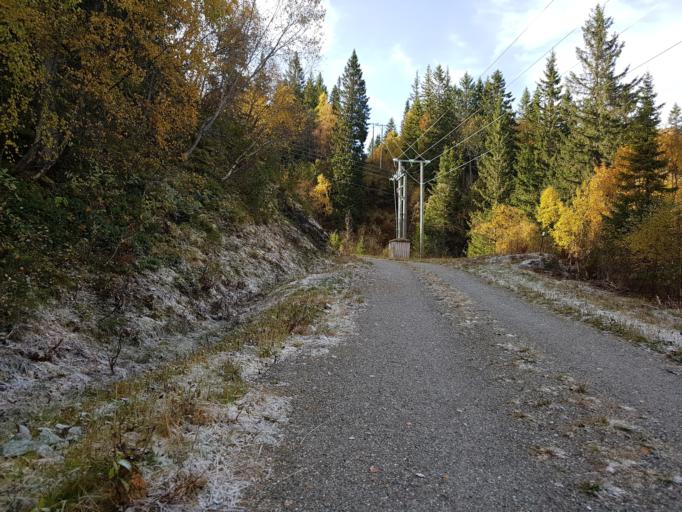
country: NO
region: Sor-Trondelag
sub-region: Trondheim
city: Trondheim
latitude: 63.4493
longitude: 10.2851
